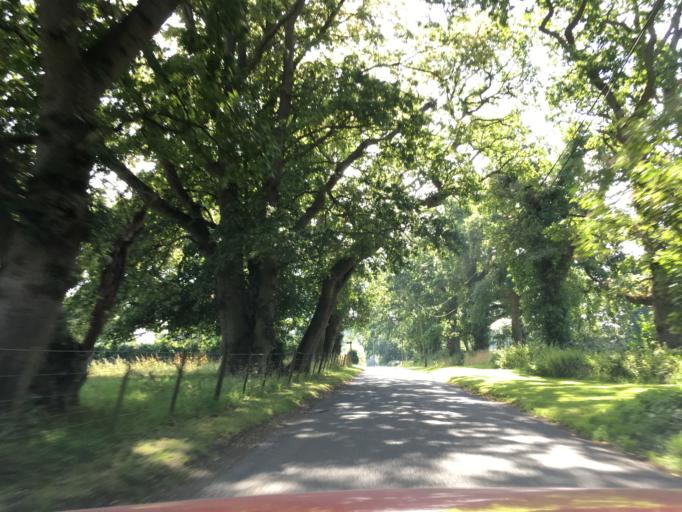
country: GB
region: England
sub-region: West Berkshire
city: Kintbury
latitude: 51.3782
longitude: -1.4461
